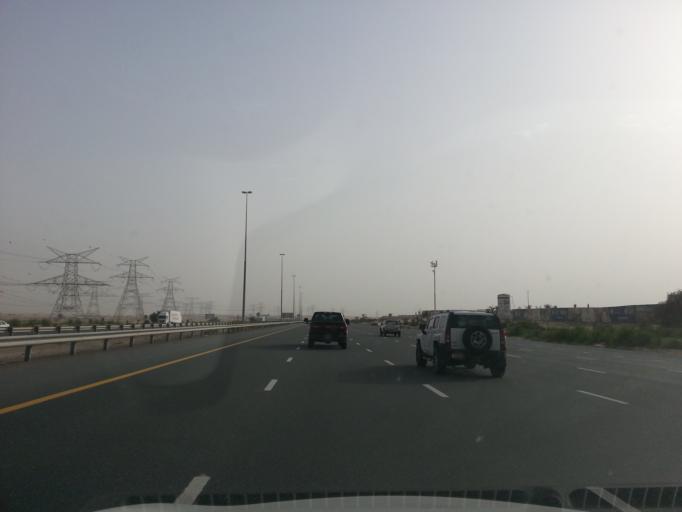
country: AE
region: Dubai
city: Dubai
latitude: 24.9977
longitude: 55.2548
